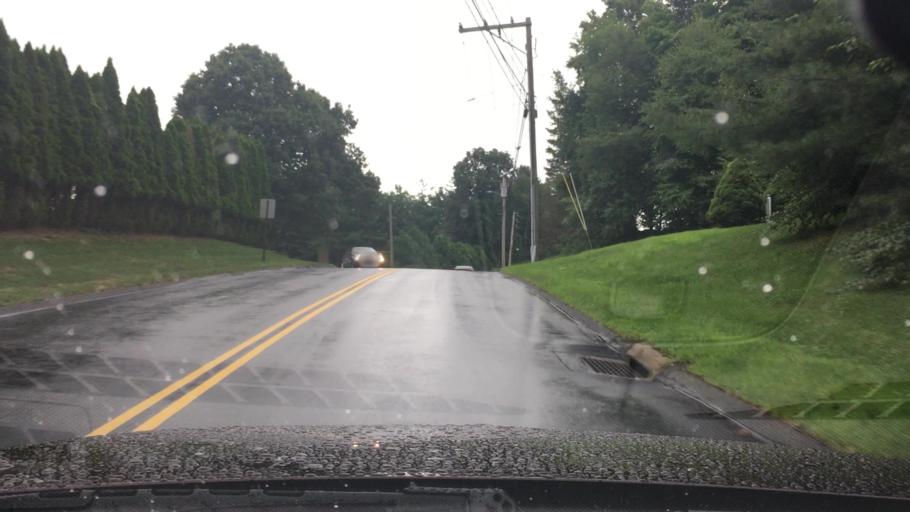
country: US
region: Connecticut
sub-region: New Haven County
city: Cheshire Village
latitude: 41.5301
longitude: -72.9174
